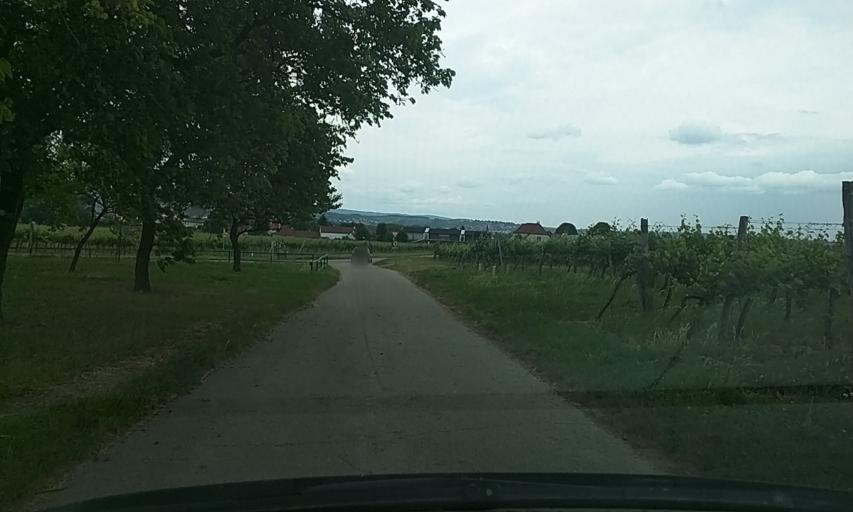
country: AT
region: Lower Austria
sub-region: Politischer Bezirk Krems
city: Weinzierl bei Krems
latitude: 48.3805
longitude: 15.6152
